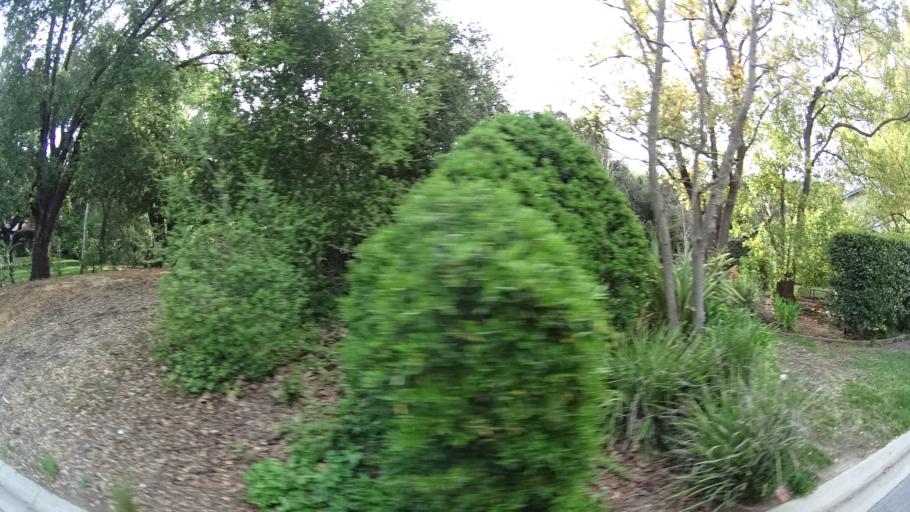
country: US
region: California
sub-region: Ventura County
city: Thousand Oaks
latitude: 34.1836
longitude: -118.8211
